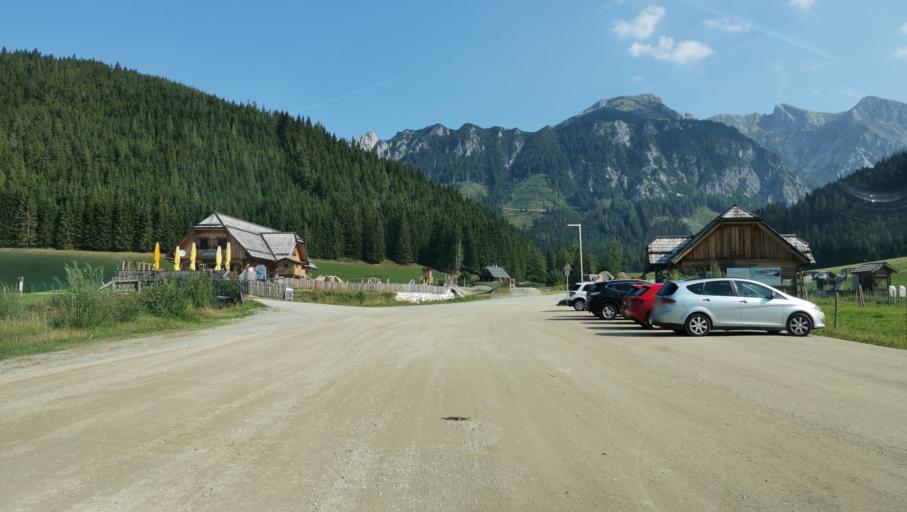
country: AT
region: Styria
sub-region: Politischer Bezirk Liezen
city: Trieben
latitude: 47.5287
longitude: 14.4846
